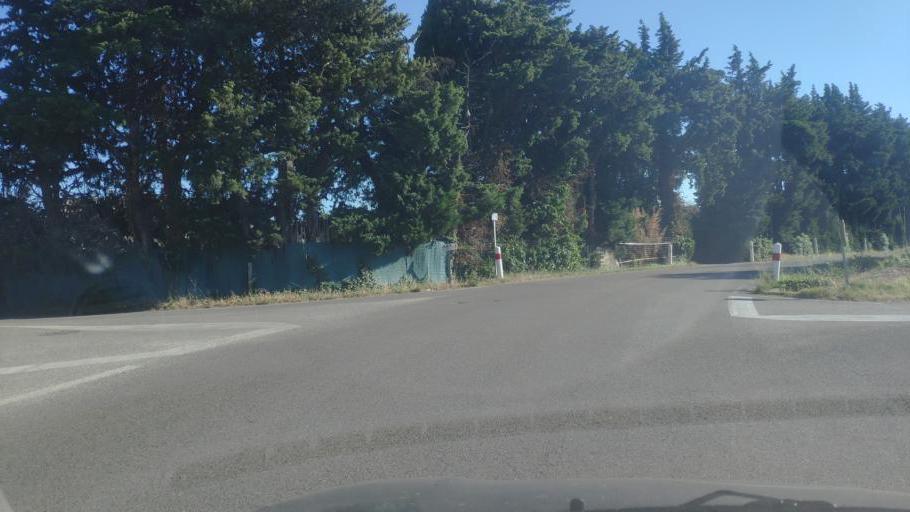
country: FR
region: Provence-Alpes-Cote d'Azur
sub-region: Departement du Vaucluse
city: Aubignan
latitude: 44.0912
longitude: 5.0253
